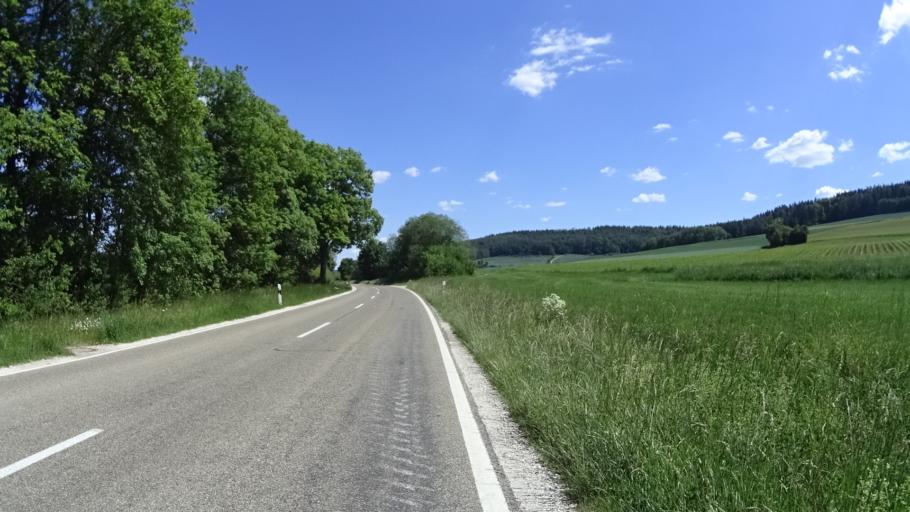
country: DE
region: Bavaria
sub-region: Regierungsbezirk Mittelfranken
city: Thalmassing
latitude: 49.0796
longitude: 11.2567
